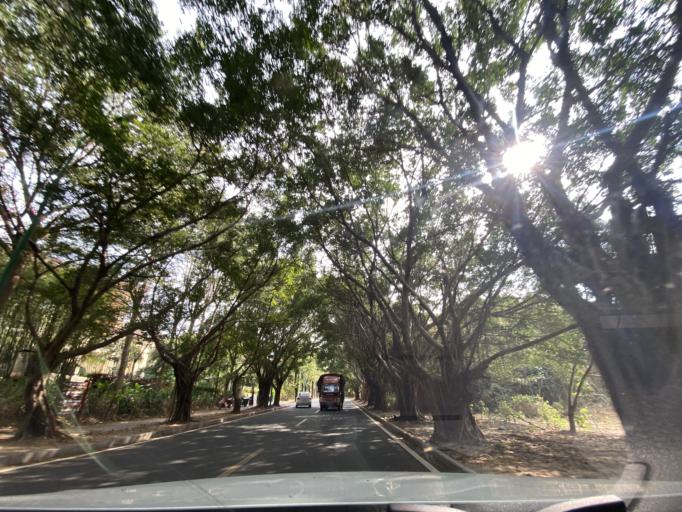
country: CN
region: Hainan
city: Tiandu
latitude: 18.2269
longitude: 109.6213
